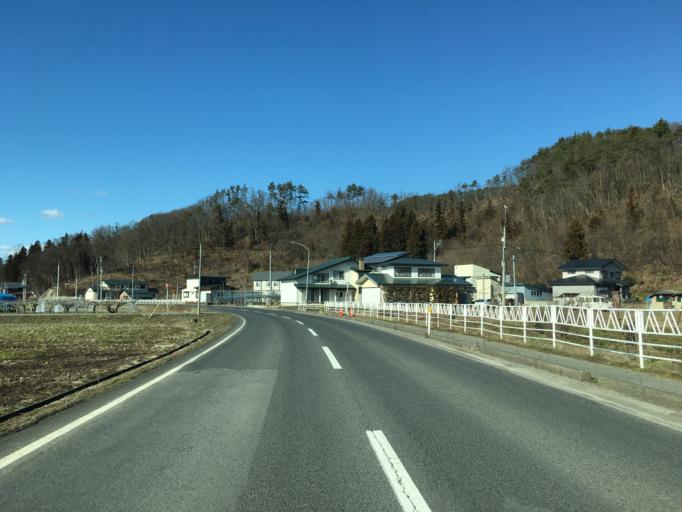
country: JP
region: Yamagata
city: Takahata
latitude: 37.9807
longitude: 140.1853
